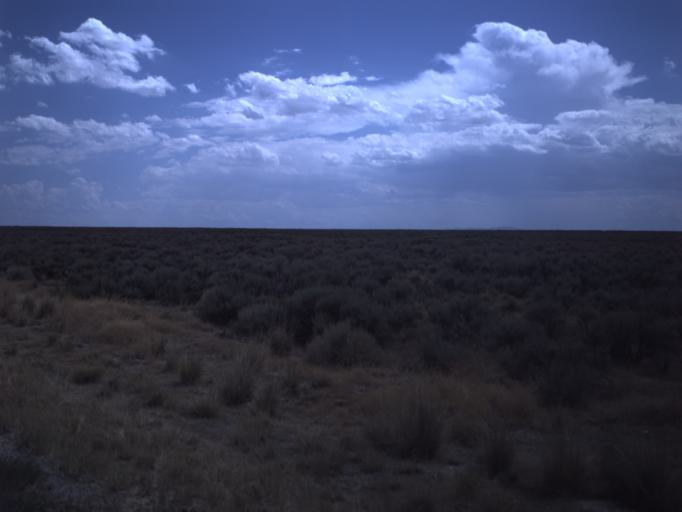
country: US
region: Utah
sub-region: Tooele County
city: Tooele
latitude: 40.3688
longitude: -112.3519
